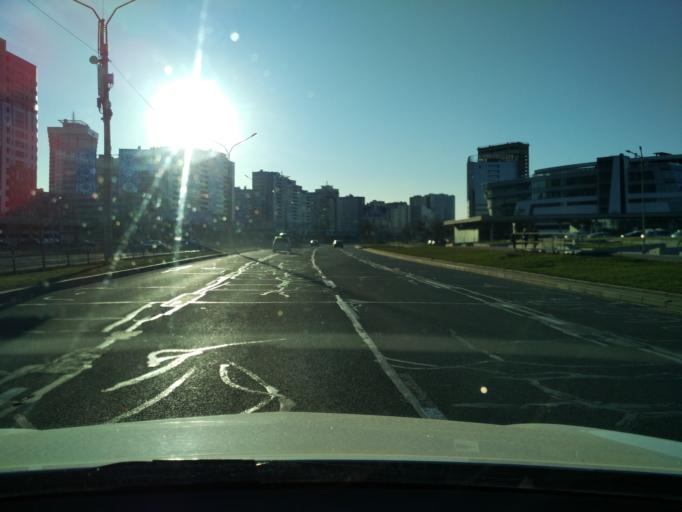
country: BY
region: Minsk
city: Zhdanovichy
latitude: 53.9379
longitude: 27.4787
